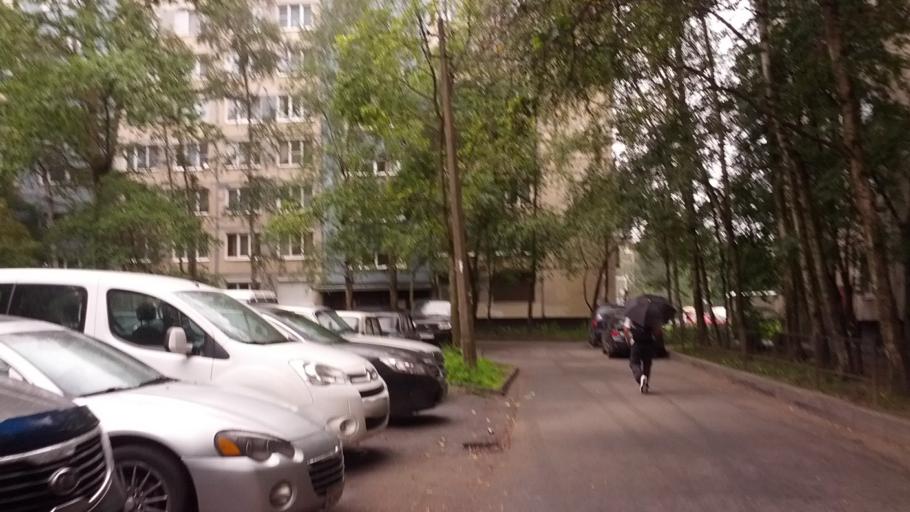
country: RU
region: St.-Petersburg
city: Obukhovo
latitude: 59.9051
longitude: 30.4710
